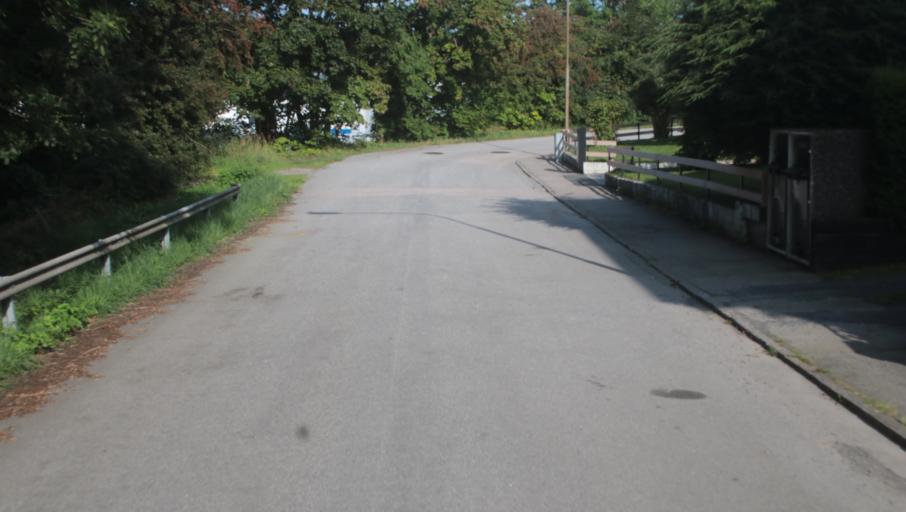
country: SE
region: Blekinge
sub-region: Karlshamns Kommun
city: Karlshamn
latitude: 56.1790
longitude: 14.8526
